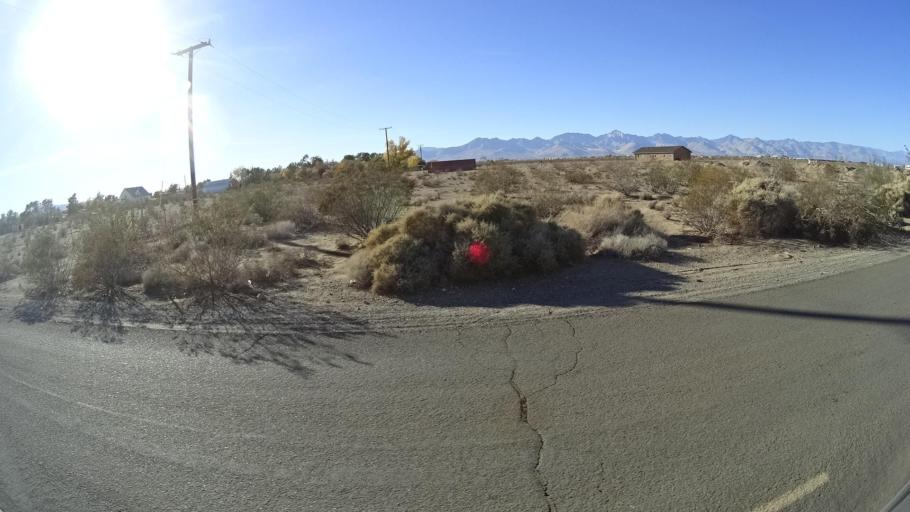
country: US
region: California
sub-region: Kern County
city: Ridgecrest
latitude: 35.6466
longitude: -117.7052
